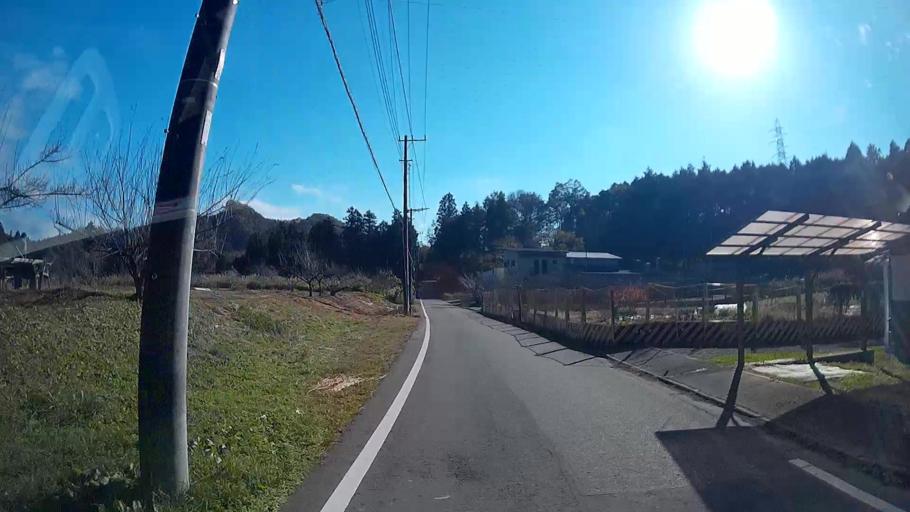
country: JP
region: Yamanashi
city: Uenohara
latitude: 35.5888
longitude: 139.1315
